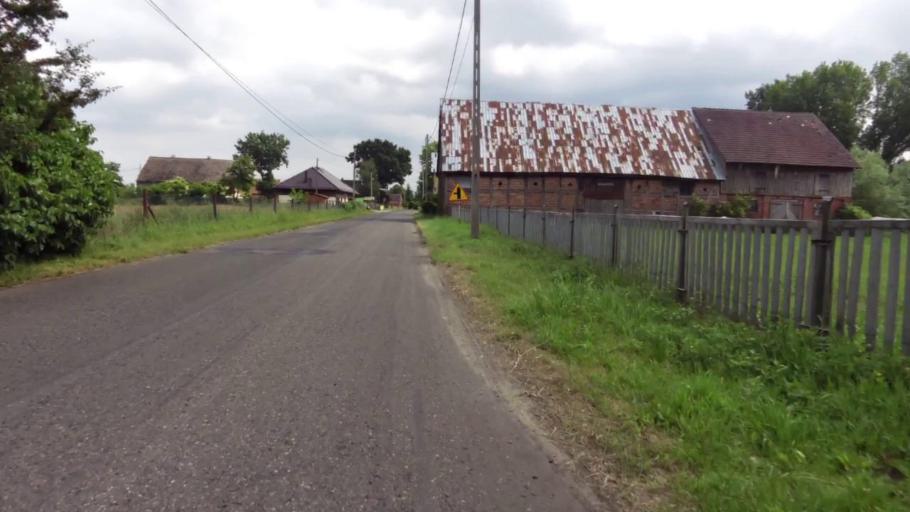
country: PL
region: West Pomeranian Voivodeship
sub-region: Powiat goleniowski
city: Stepnica
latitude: 53.6733
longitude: 14.5701
